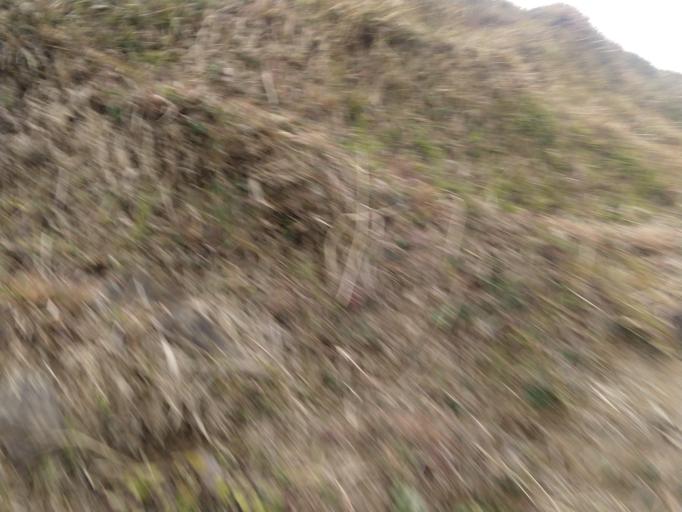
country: IN
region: Himachal Pradesh
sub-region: Kangra
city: Dharmsala
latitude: 32.2191
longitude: 76.3348
